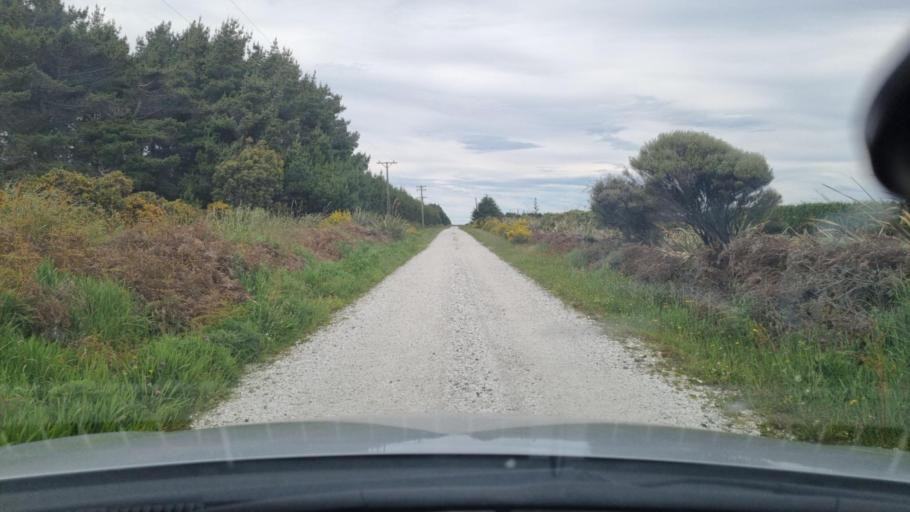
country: NZ
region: Southland
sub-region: Invercargill City
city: Bluff
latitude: -46.5121
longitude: 168.3529
